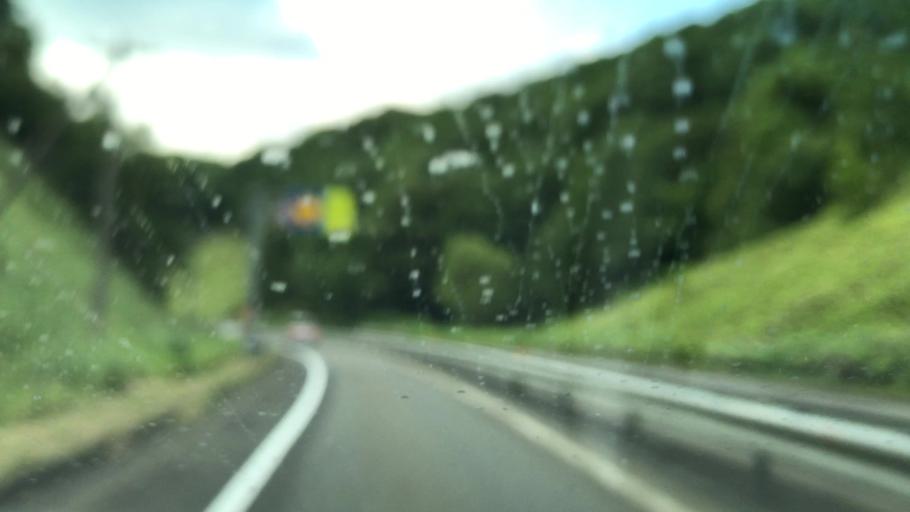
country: JP
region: Hokkaido
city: Shimo-furano
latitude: 42.8859
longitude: 142.2626
